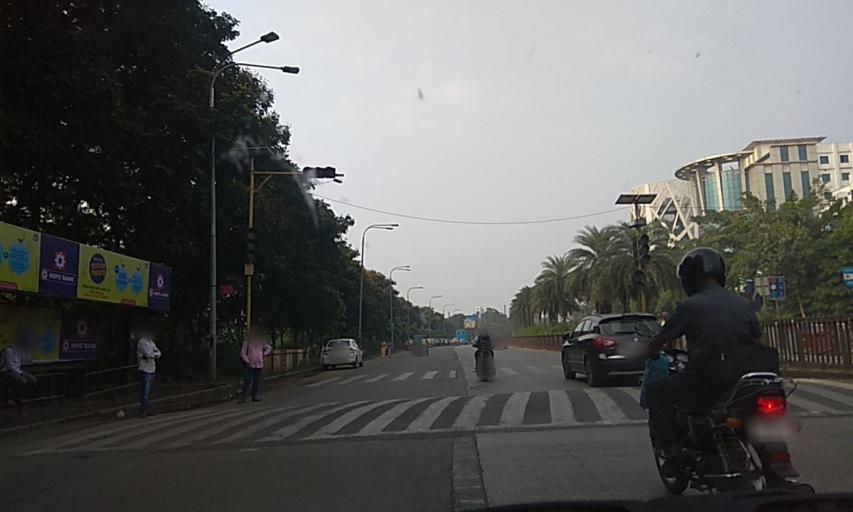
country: IN
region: Maharashtra
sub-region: Pune Division
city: Khadki
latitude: 18.5482
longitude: 73.8922
